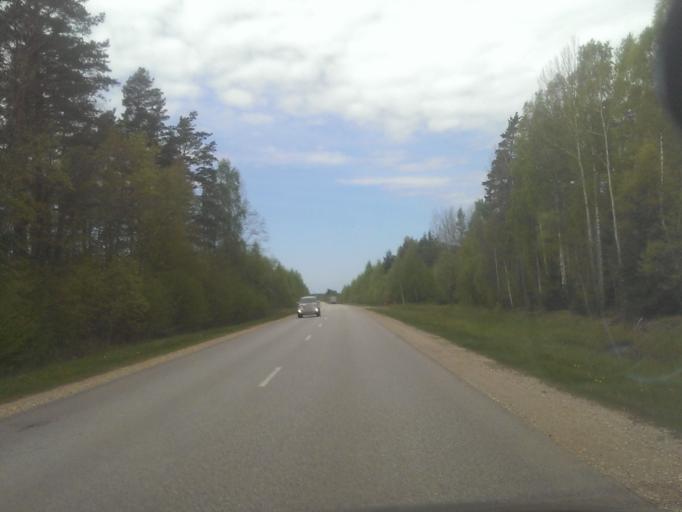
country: LV
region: Ventspils Rajons
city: Piltene
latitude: 57.1654
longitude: 21.6831
